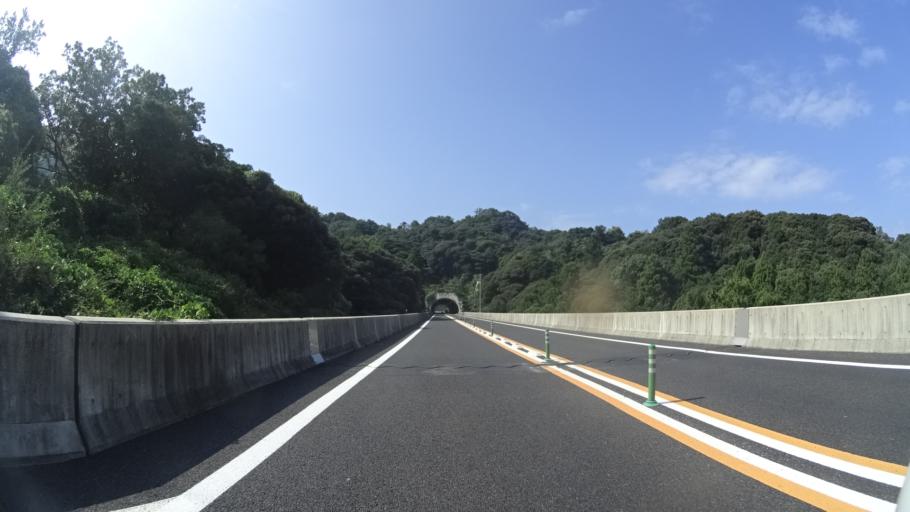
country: JP
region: Shimane
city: Odacho-oda
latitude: 35.1215
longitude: 132.3892
